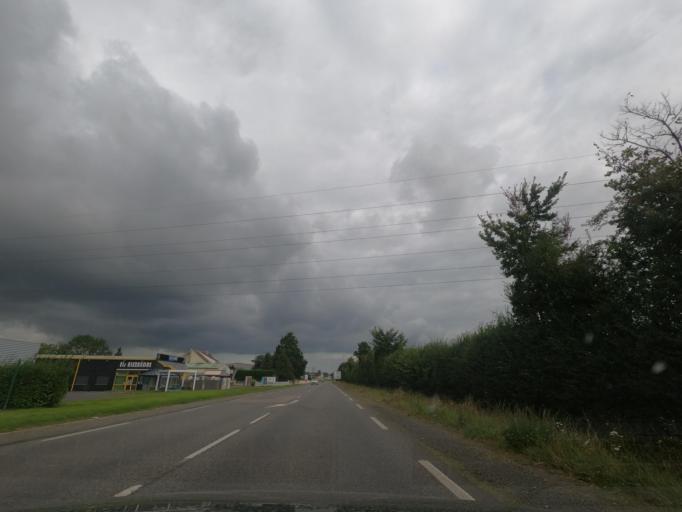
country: FR
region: Lower Normandy
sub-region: Departement de l'Orne
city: Argentan
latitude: 48.7490
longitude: 0.0041
